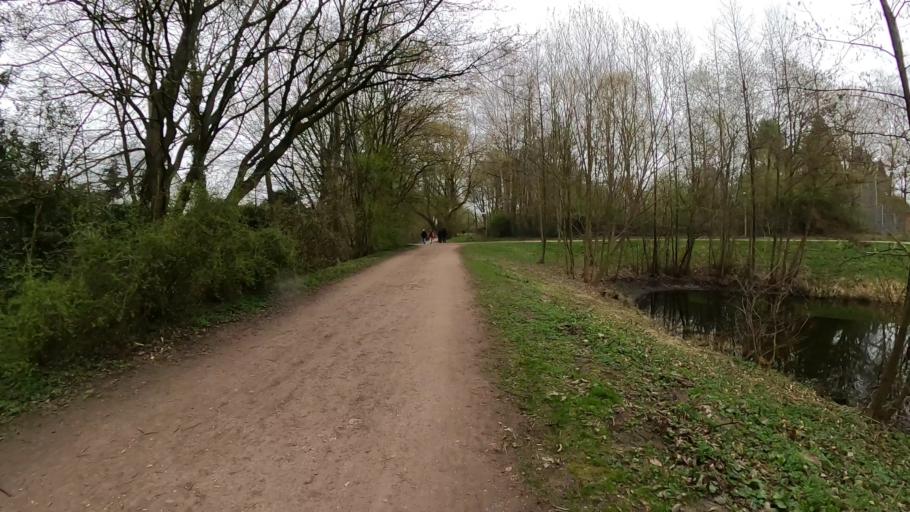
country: DE
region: Hamburg
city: Langenhorn
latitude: 53.6730
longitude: 9.9916
